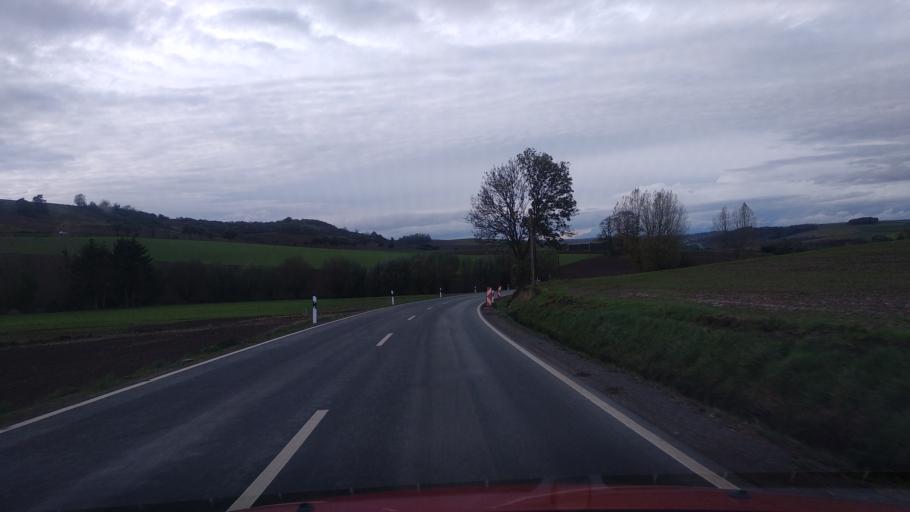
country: DE
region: North Rhine-Westphalia
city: Brakel
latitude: 51.6741
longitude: 9.2305
